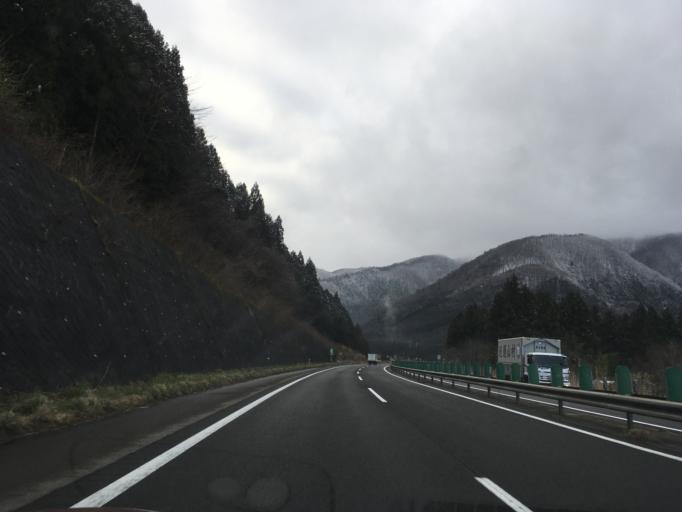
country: JP
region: Miyagi
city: Shiroishi
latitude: 38.2012
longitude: 140.5817
